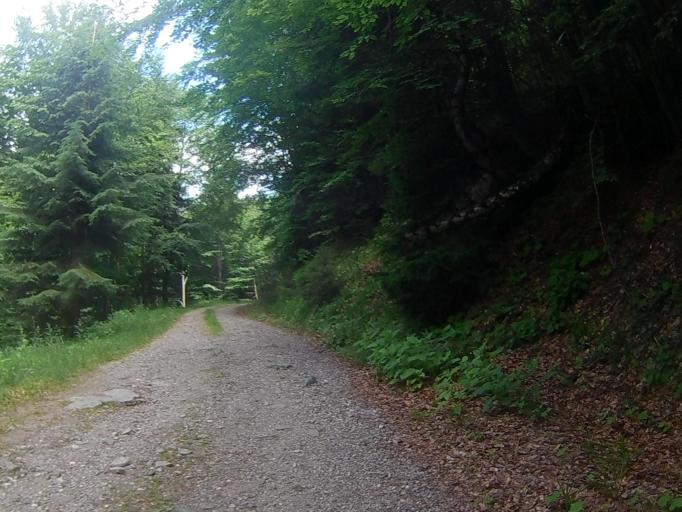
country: SI
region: Selnica ob Dravi
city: Selnica ob Dravi
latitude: 46.5077
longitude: 15.4832
